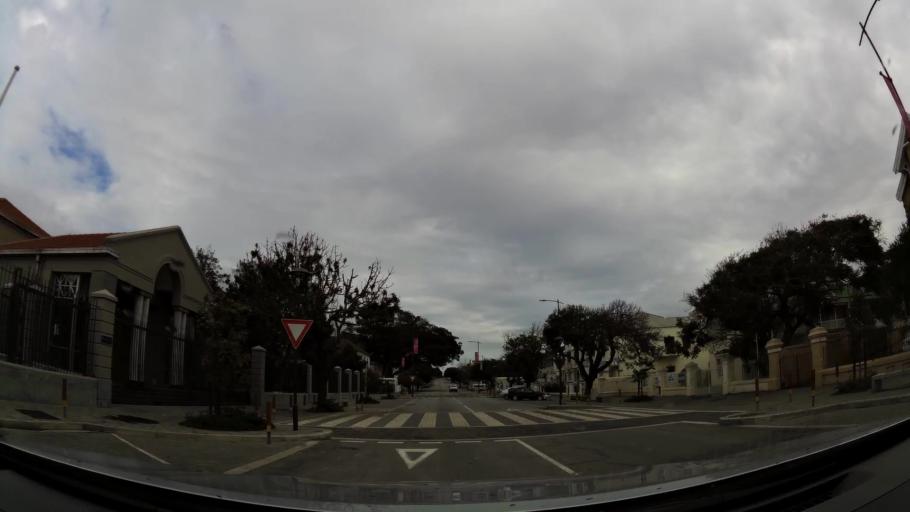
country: ZA
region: Eastern Cape
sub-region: Nelson Mandela Bay Metropolitan Municipality
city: Port Elizabeth
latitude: -33.9642
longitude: 25.6192
